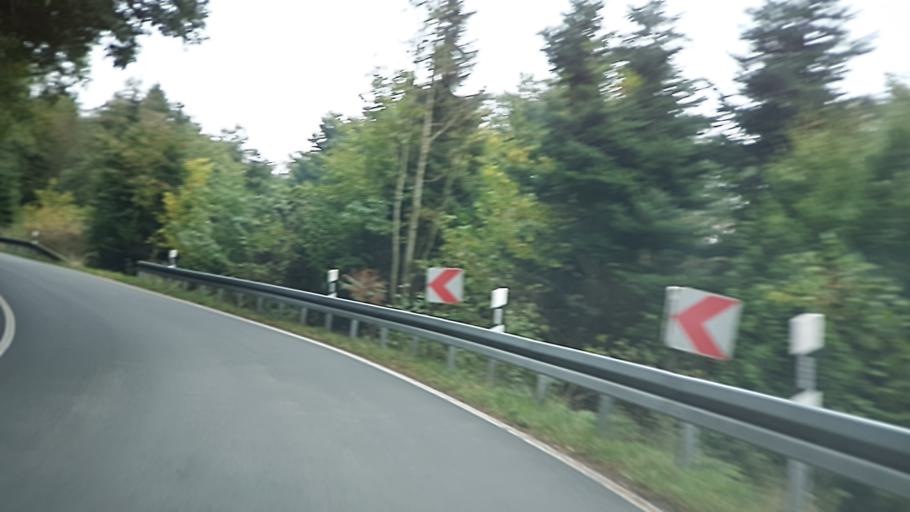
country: DE
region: North Rhine-Westphalia
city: Meinerzhagen
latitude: 51.1312
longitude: 7.6489
